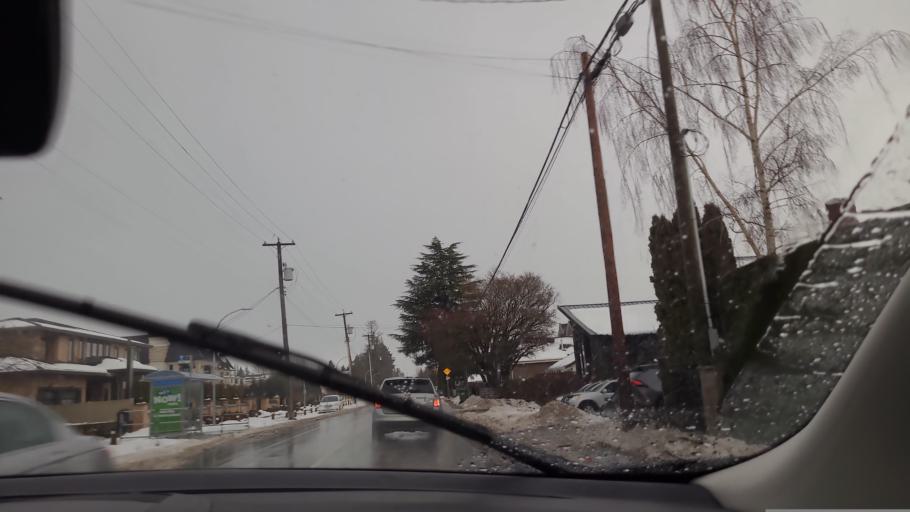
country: CA
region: British Columbia
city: Richmond
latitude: 49.1310
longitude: -123.1590
